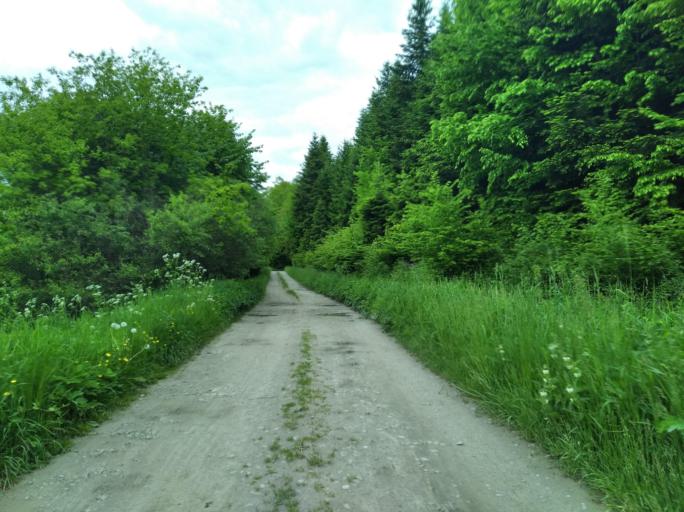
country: PL
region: Subcarpathian Voivodeship
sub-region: Powiat brzozowski
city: Jasionow
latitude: 49.6701
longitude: 21.9845
